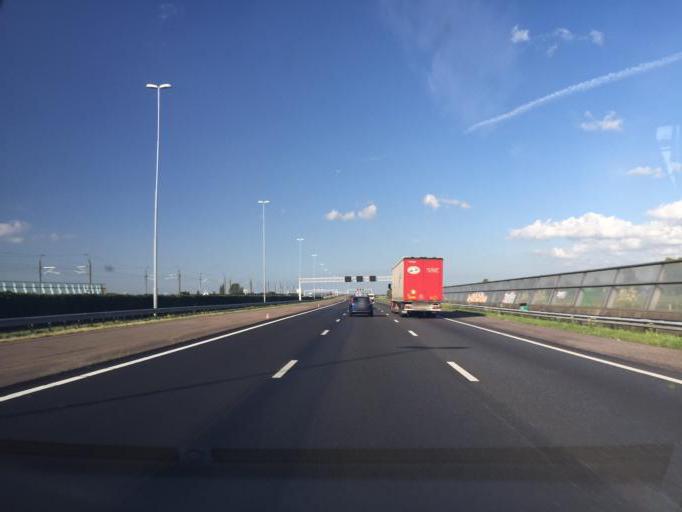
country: NL
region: South Holland
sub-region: Gemeente Leiderdorp
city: Leiderdorp
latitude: 52.1772
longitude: 4.5825
